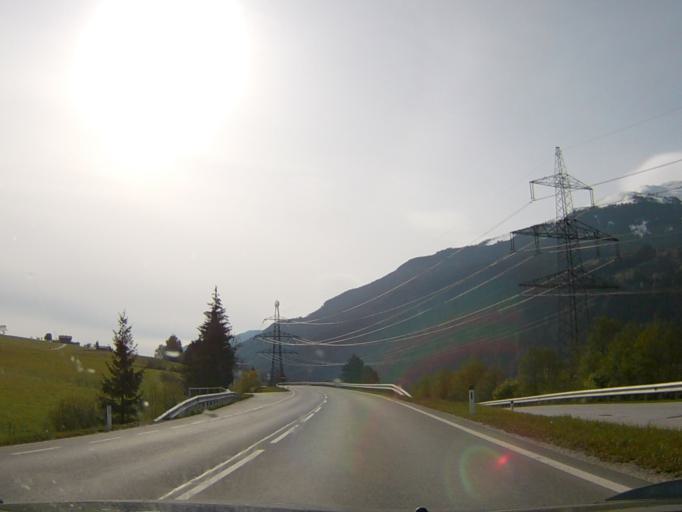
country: AT
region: Salzburg
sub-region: Politischer Bezirk Zell am See
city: Hollersbach im Pinzgau
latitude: 47.2817
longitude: 12.4041
